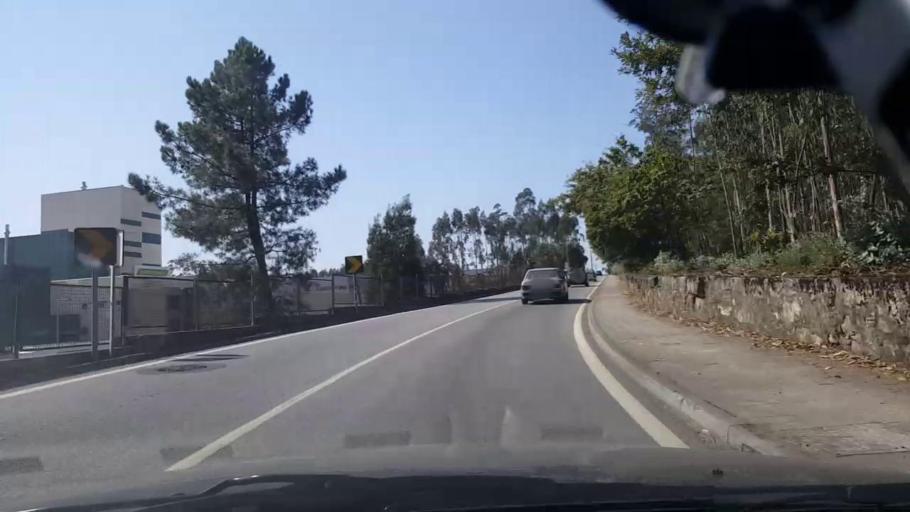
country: PT
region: Porto
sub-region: Povoa de Varzim
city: Pedroso
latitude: 41.4089
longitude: -8.6682
